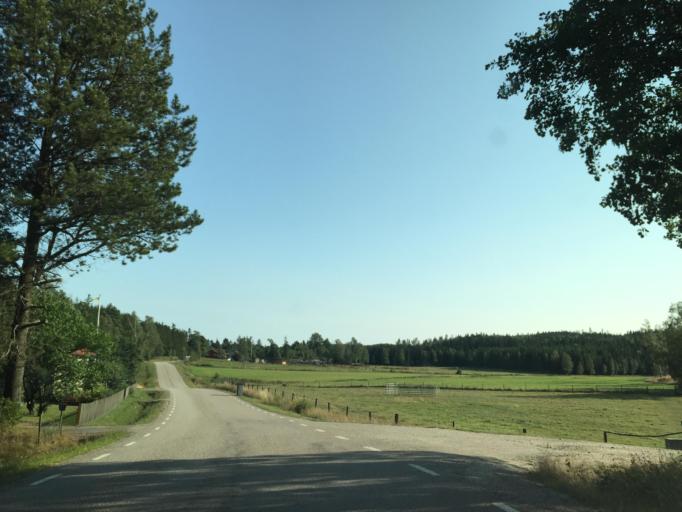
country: SE
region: Vaestra Goetaland
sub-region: Lilla Edets Kommun
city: Lilla Edet
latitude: 58.1651
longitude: 12.0715
